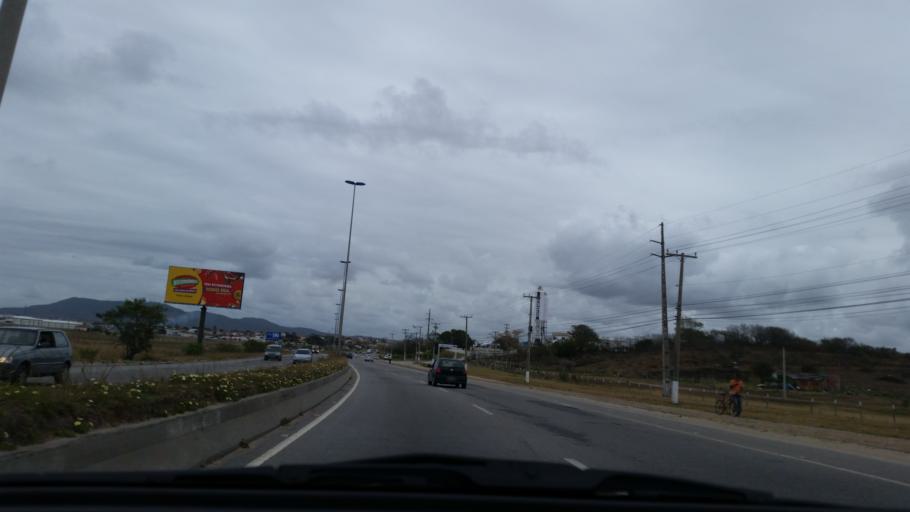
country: BR
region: Rio de Janeiro
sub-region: Sao Pedro Da Aldeia
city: Sao Pedro da Aldeia
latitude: -22.8340
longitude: -42.0799
